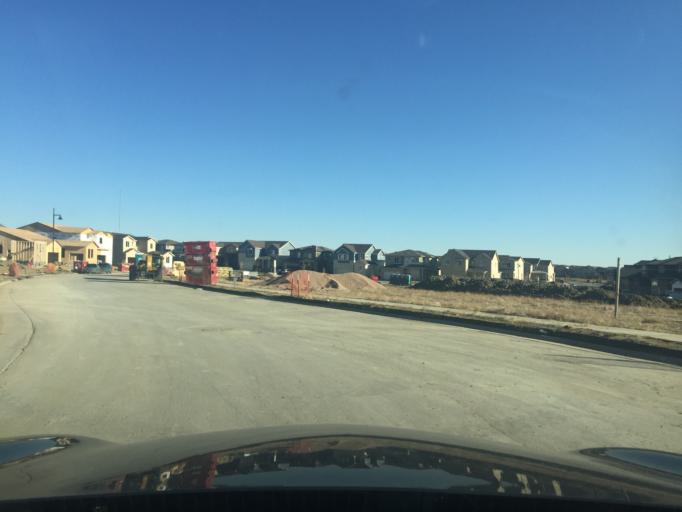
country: US
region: Colorado
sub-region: Boulder County
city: Erie
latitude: 40.0502
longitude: -105.0361
